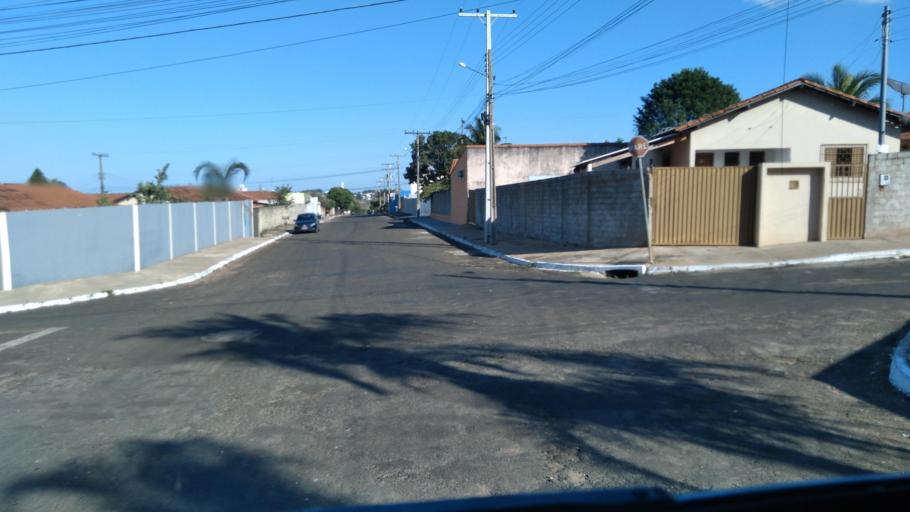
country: BR
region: Goias
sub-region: Mineiros
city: Mineiros
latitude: -17.5544
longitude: -52.5474
